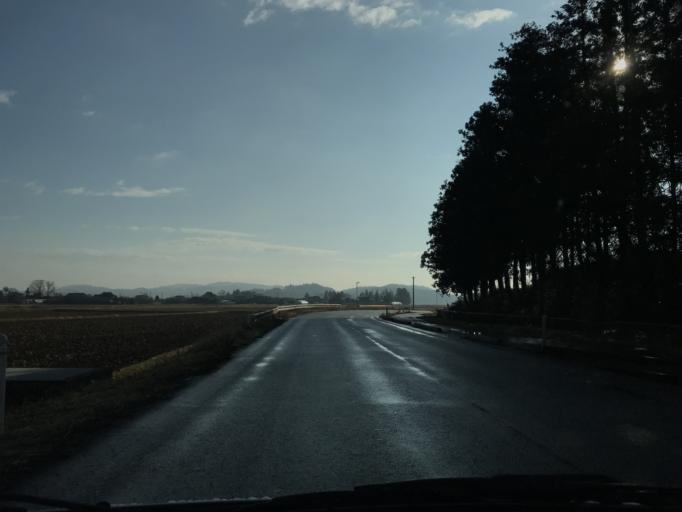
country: JP
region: Iwate
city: Ichinoseki
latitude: 38.7716
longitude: 141.1784
